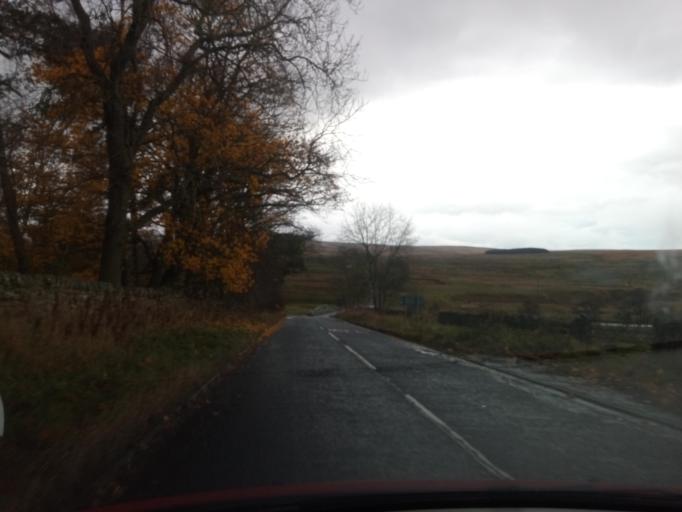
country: GB
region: England
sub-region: Northumberland
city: Rochester
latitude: 55.2510
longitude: -2.2207
